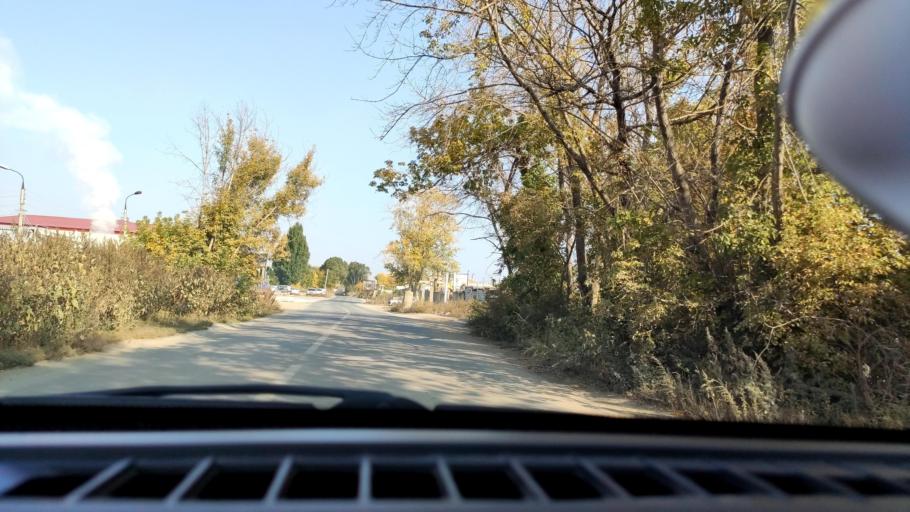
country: RU
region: Samara
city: Samara
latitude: 53.1908
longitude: 50.2675
